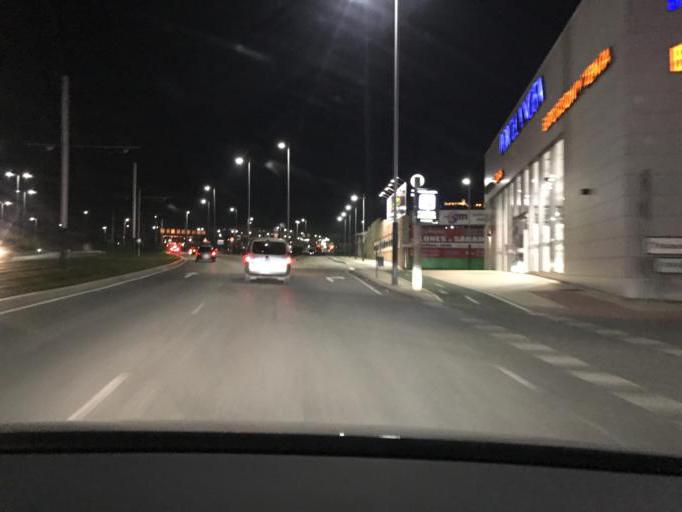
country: ES
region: Andalusia
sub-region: Provincia de Jaen
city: Jaen
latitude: 37.7930
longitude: -3.7807
